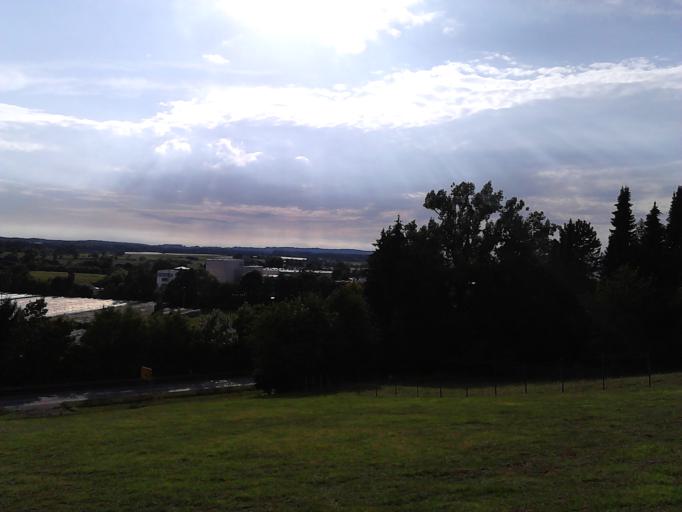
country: DE
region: Baden-Wuerttemberg
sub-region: Tuebingen Region
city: Markdorf
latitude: 47.7071
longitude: 9.4103
